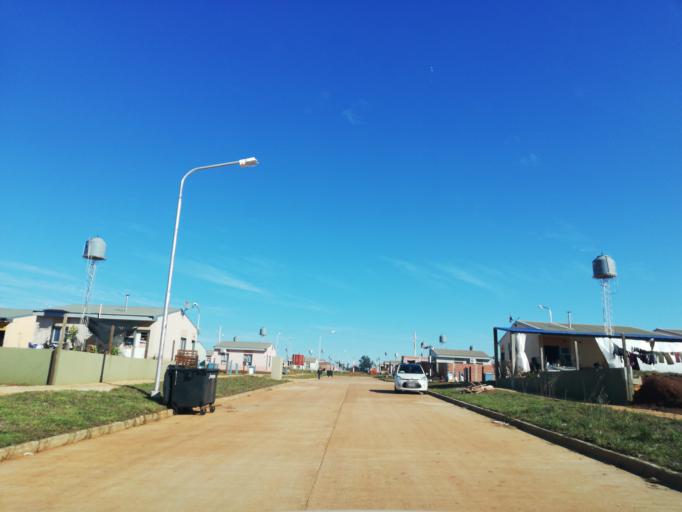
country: AR
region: Misiones
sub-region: Departamento de Capital
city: Posadas
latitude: -27.4128
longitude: -55.9901
